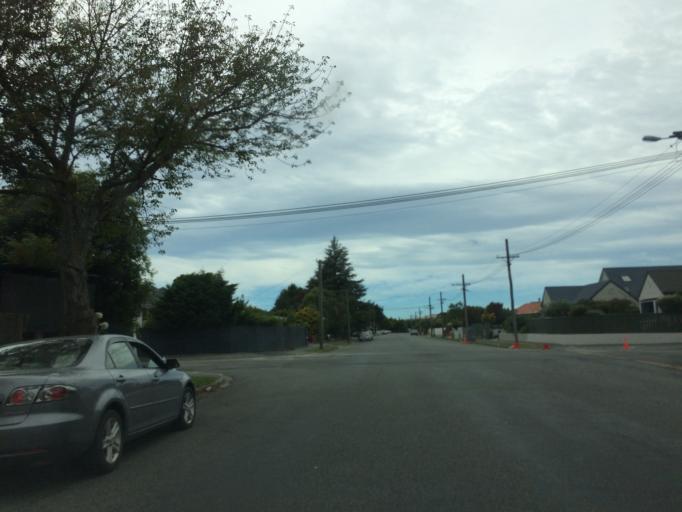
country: NZ
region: Canterbury
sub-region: Selwyn District
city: Prebbleton
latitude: -43.5203
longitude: 172.5586
